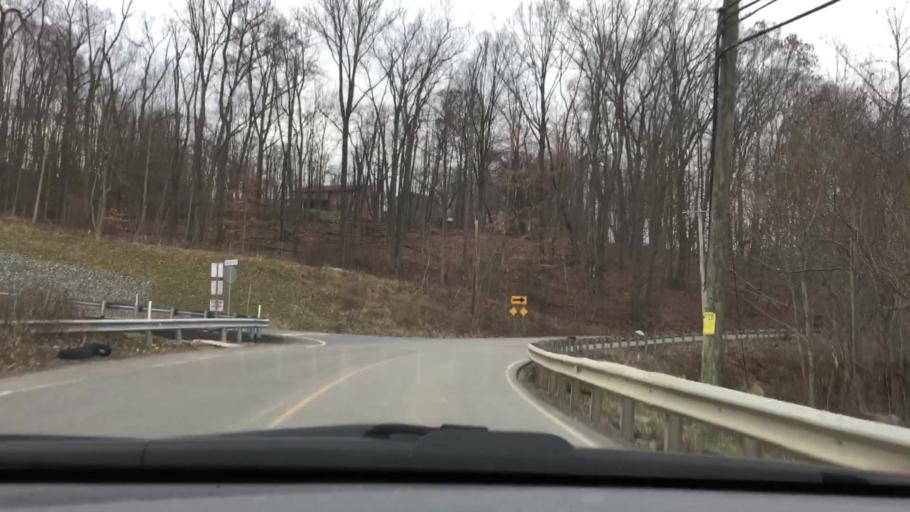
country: US
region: Pennsylvania
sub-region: Washington County
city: McDonald
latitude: 40.3585
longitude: -80.2358
